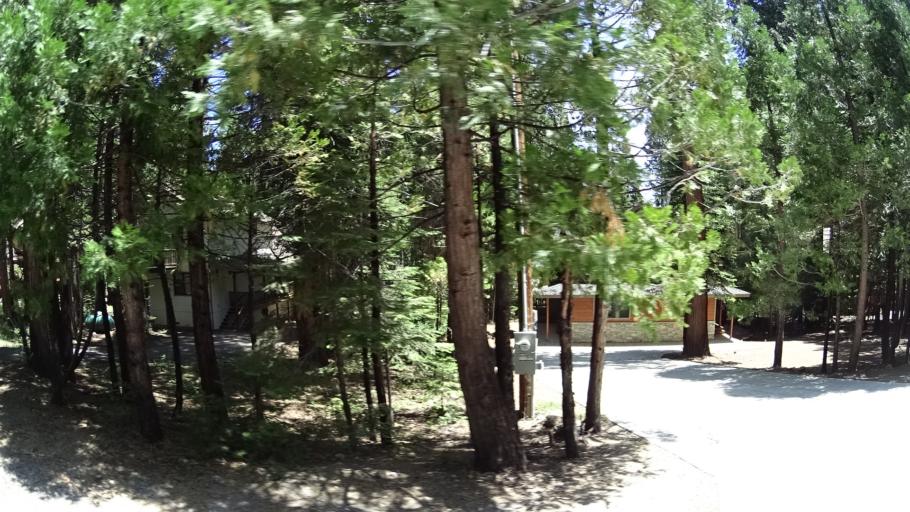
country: US
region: California
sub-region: Calaveras County
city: Arnold
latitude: 38.3082
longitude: -120.2577
